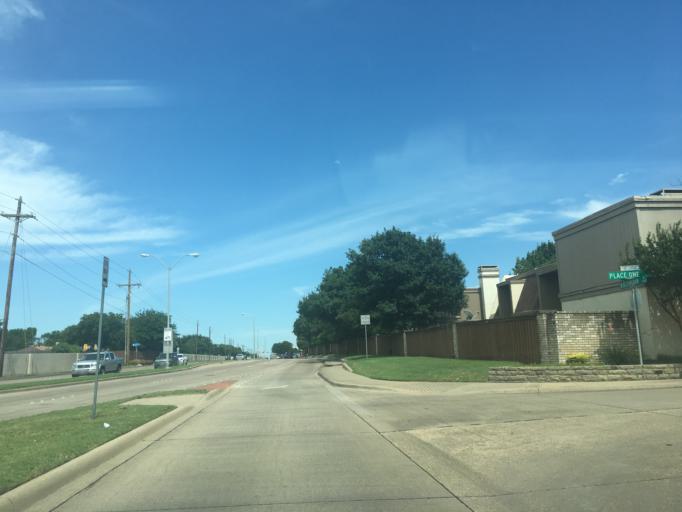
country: US
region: Texas
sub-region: Dallas County
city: Richardson
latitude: 32.9312
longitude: -96.7055
